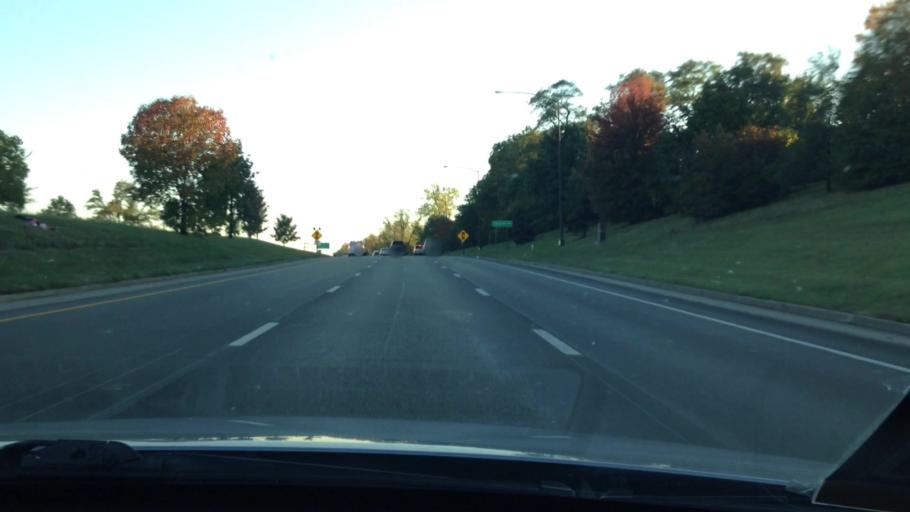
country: US
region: Kansas
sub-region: Johnson County
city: Westwood
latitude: 39.0324
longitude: -94.5537
